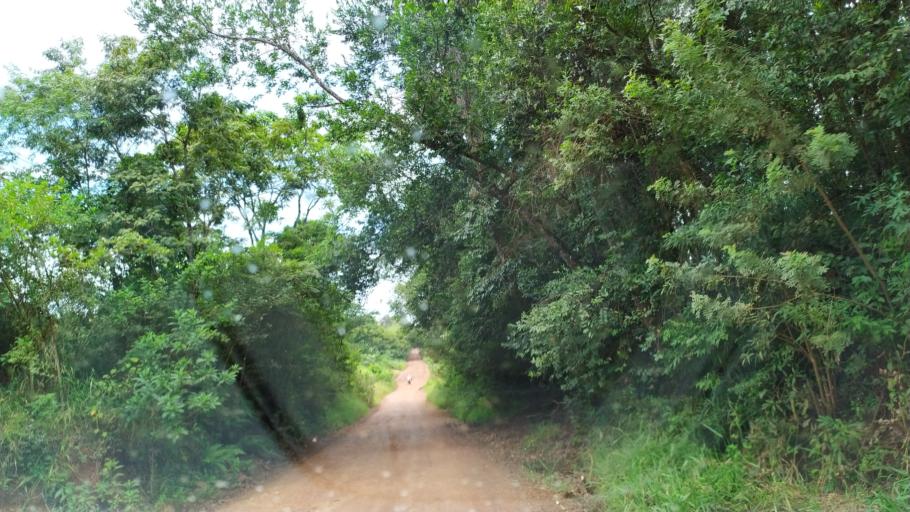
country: AR
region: Misiones
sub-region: Departamento de Eldorado
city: Eldorado
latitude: -26.4298
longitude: -54.6046
